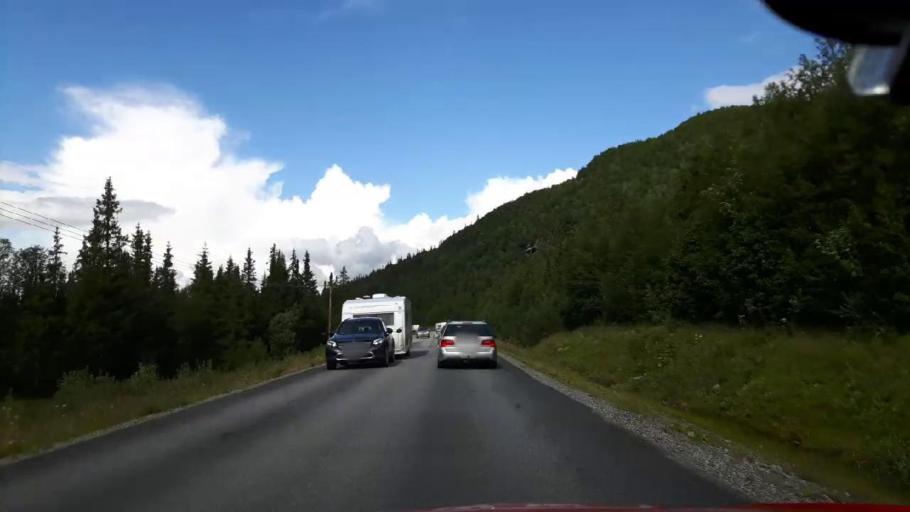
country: SE
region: Vaesterbotten
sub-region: Vilhelmina Kommun
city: Sjoberg
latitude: 65.0358
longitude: 15.1349
